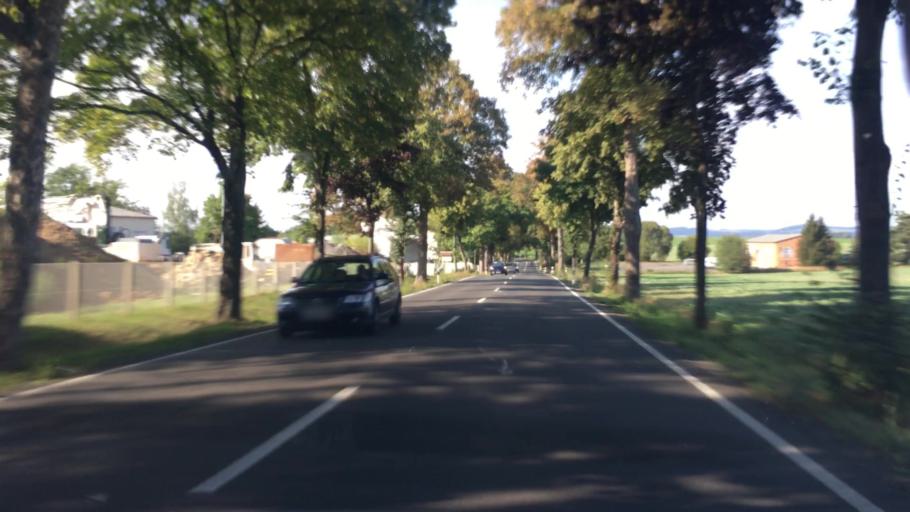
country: DE
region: Saxony
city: Dohma
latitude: 50.9140
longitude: 13.9448
